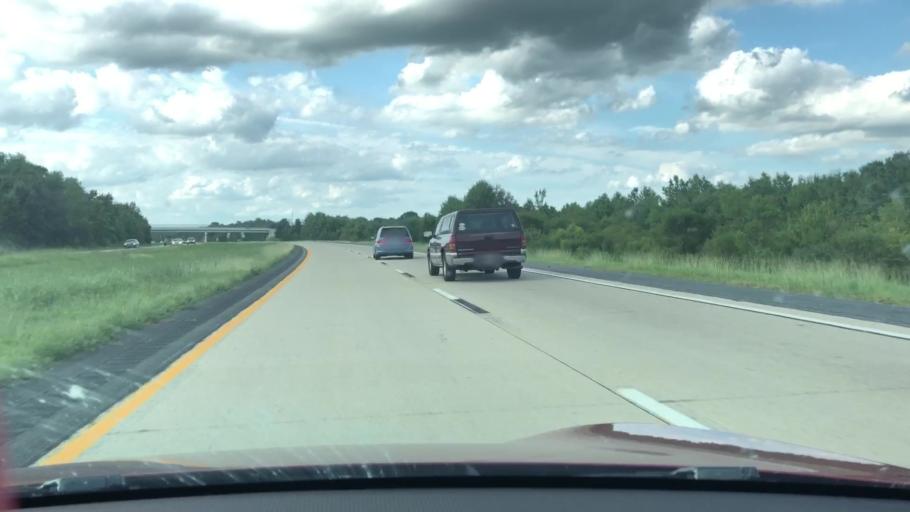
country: US
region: Delaware
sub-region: Kent County
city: Smyrna
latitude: 39.3014
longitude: -75.5915
